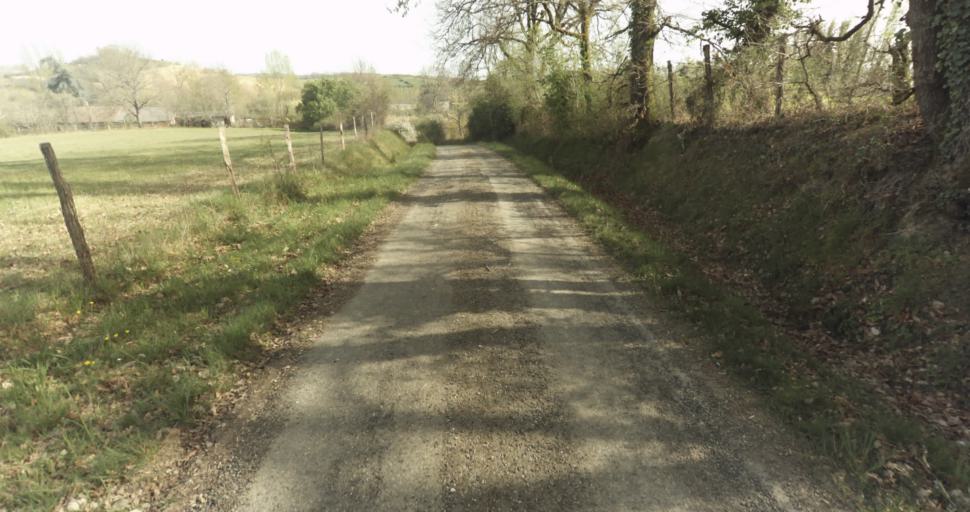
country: FR
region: Midi-Pyrenees
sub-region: Departement du Tarn-et-Garonne
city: Lafrancaise
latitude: 44.1471
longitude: 1.1761
